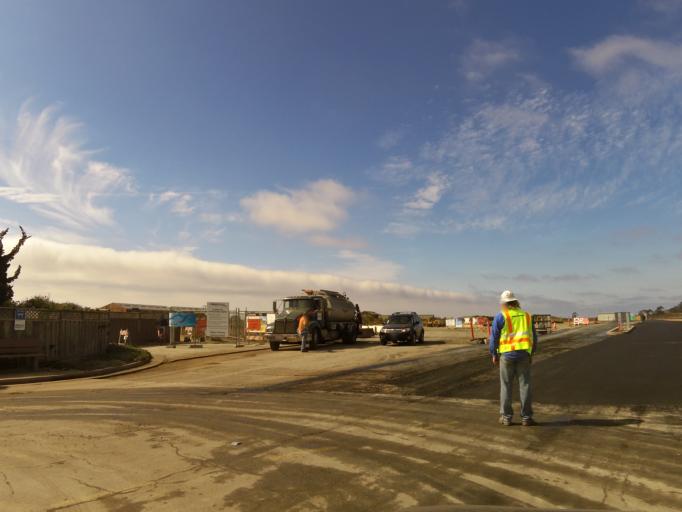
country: US
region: California
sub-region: Santa Cruz County
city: Santa Cruz
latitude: 36.9547
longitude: -122.0623
